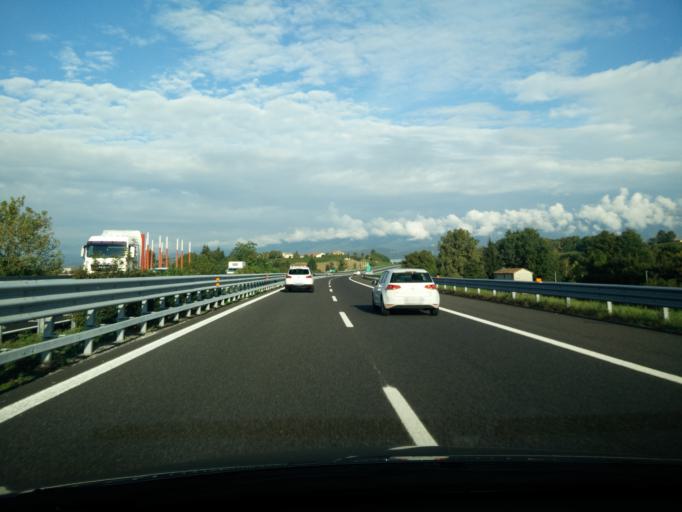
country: IT
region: Veneto
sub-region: Provincia di Treviso
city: San Martino
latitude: 45.9098
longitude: 12.3391
